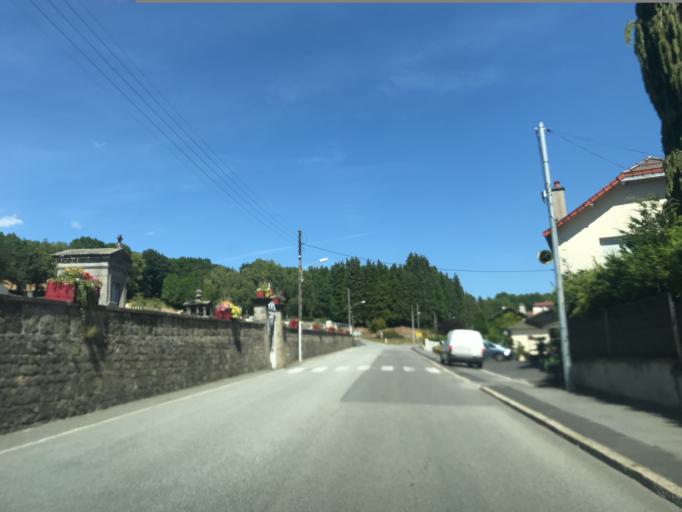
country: FR
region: Limousin
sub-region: Departement de la Creuse
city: Felletin
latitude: 45.8883
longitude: 2.1756
